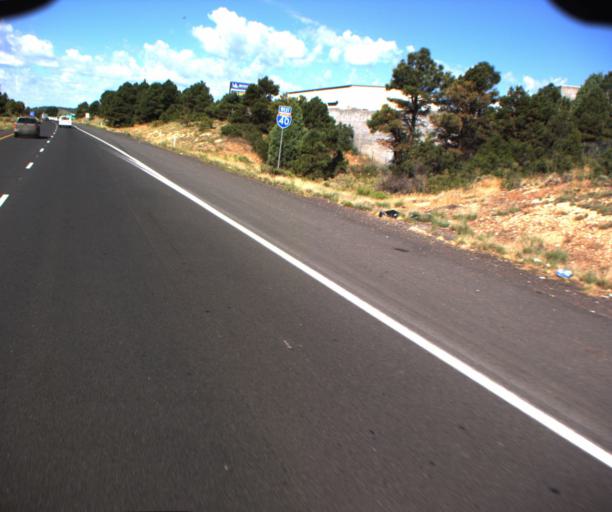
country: US
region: Arizona
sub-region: Coconino County
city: Flagstaff
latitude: 35.2147
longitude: -111.5891
